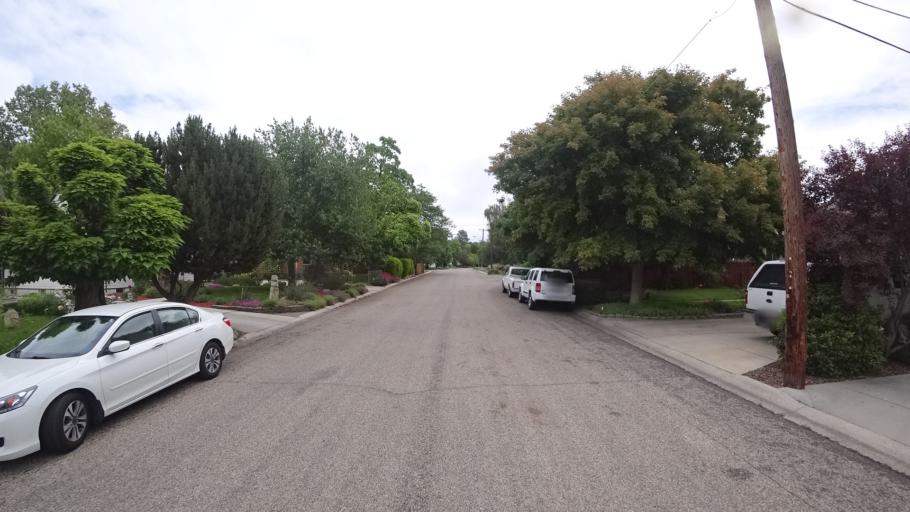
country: US
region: Idaho
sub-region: Ada County
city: Garden City
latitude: 43.6080
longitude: -116.2251
